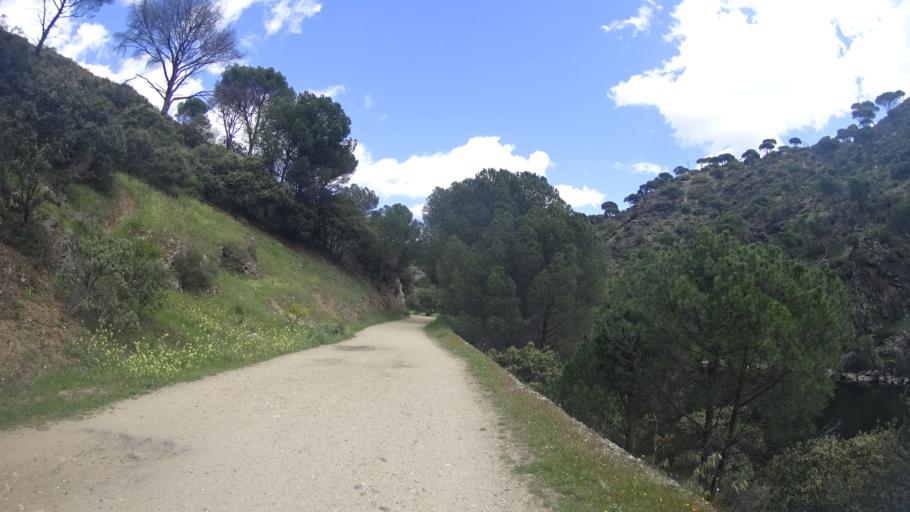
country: ES
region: Madrid
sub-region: Provincia de Madrid
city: Pelayos de la Presa
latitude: 40.3640
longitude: -4.2980
